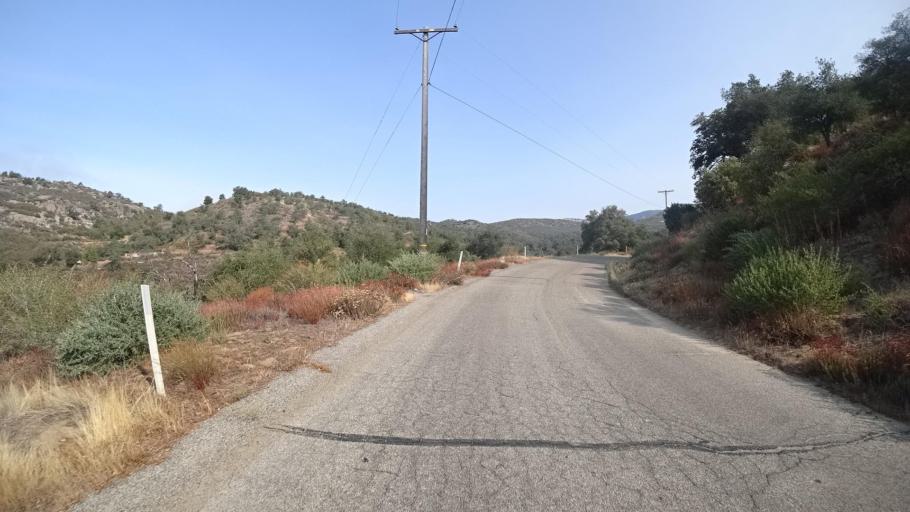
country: US
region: California
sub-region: San Diego County
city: Julian
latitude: 33.1013
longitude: -116.6593
